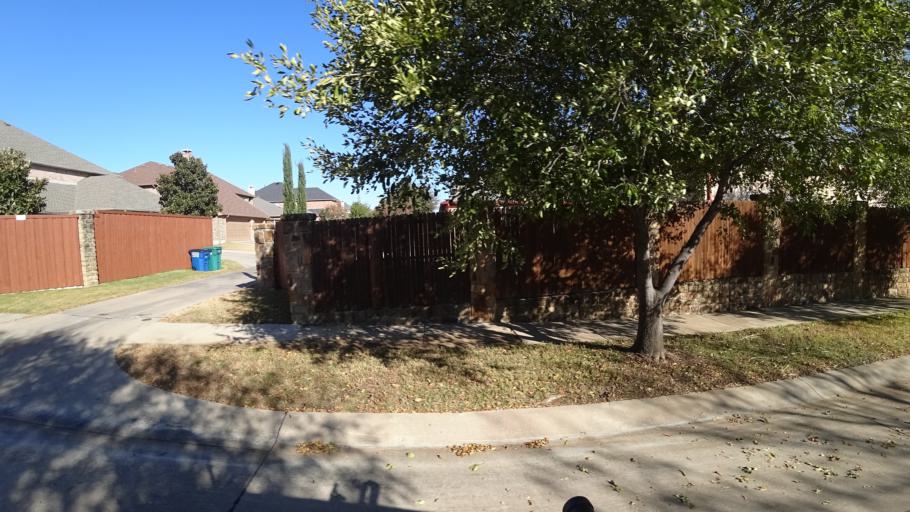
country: US
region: Texas
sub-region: Denton County
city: The Colony
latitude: 33.0383
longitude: -96.9132
